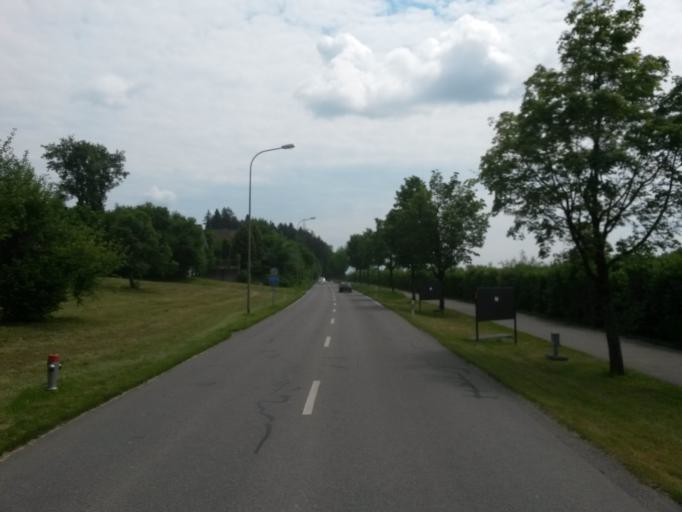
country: CH
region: Zurich
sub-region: Bezirk Pfaeffikon
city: Illnau / Unter-Illnau
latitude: 47.4048
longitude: 8.7288
